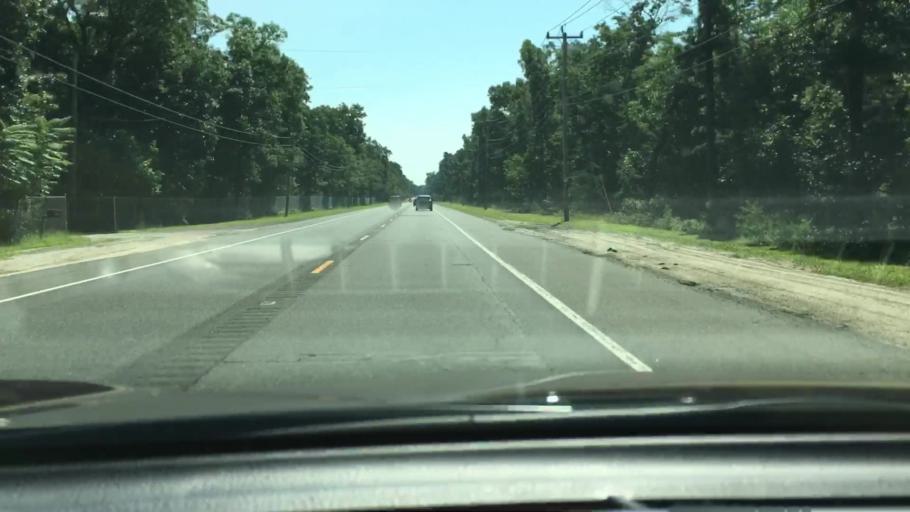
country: US
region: New Jersey
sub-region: Cumberland County
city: Laurel Lake
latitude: 39.3783
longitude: -74.9615
